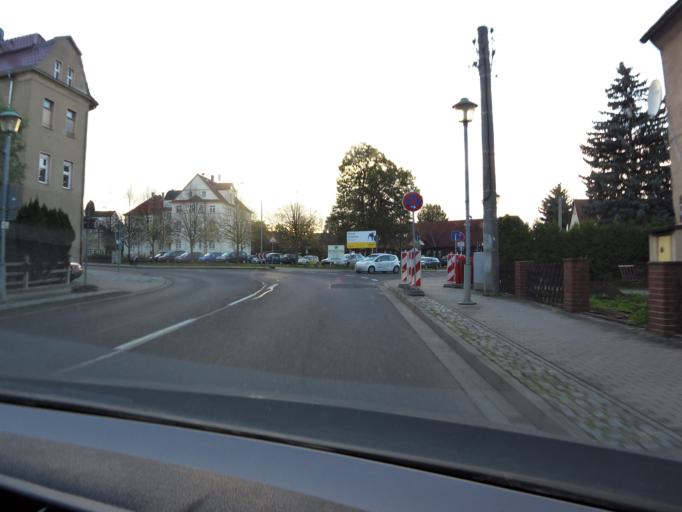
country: DE
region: Saxony
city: Rackwitz
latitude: 51.3931
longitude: 12.3294
